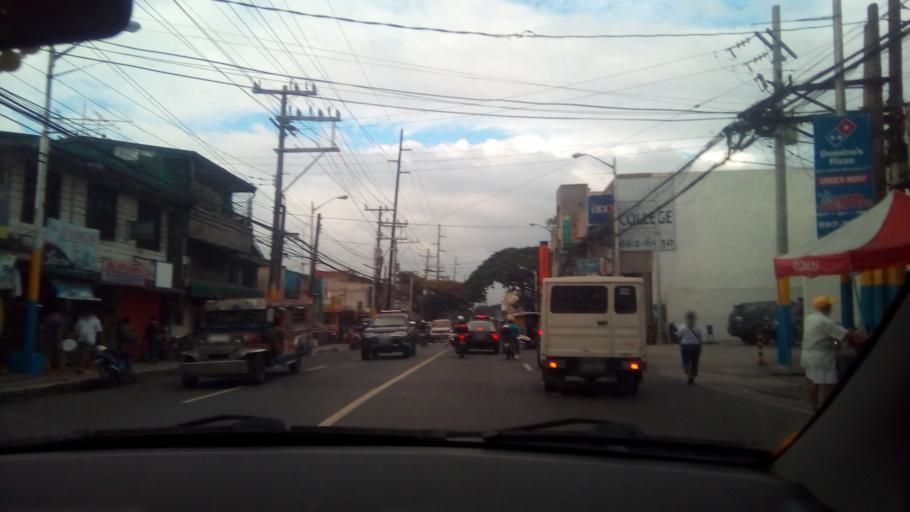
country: PH
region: Calabarzon
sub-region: Province of Laguna
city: San Pedro
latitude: 14.3910
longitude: 121.0445
